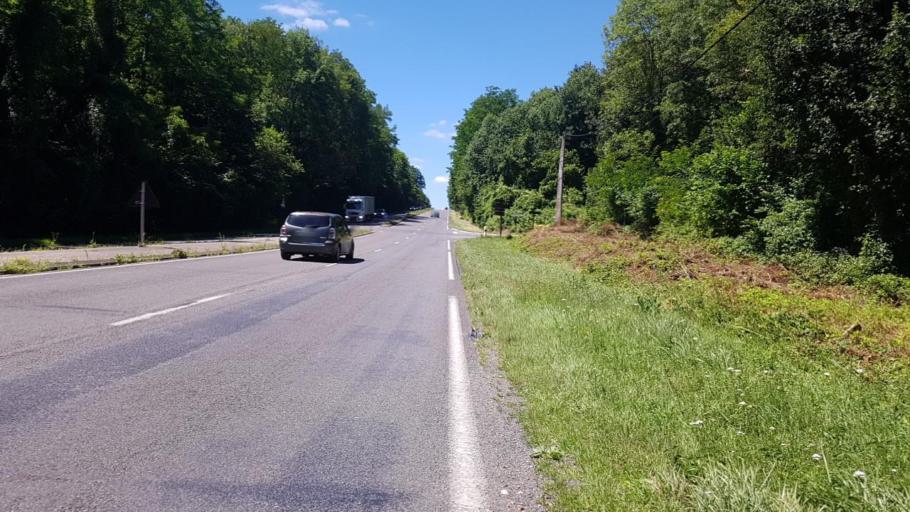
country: FR
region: Ile-de-France
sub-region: Departement de Seine-et-Marne
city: Saint-Jean-les-Deux-Jumeaux
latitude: 48.9594
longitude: 2.9984
